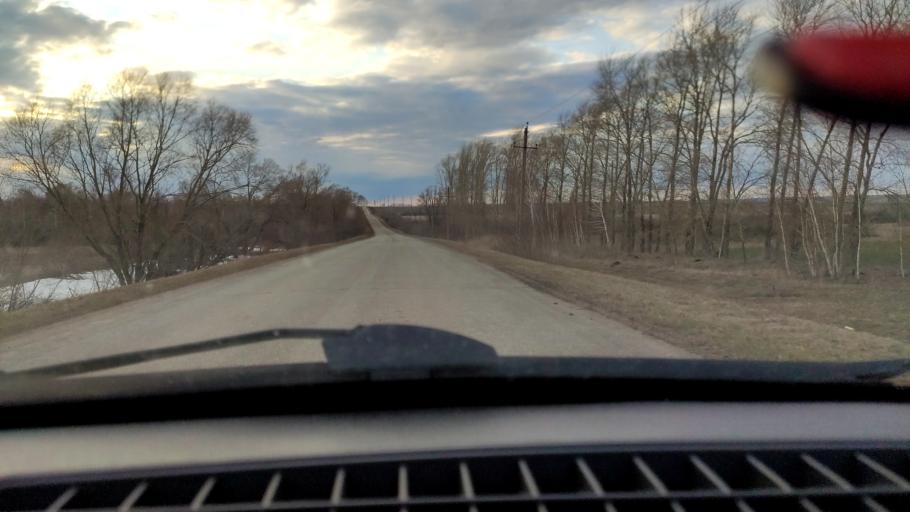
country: RU
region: Bashkortostan
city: Tolbazy
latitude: 53.9987
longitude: 55.7711
